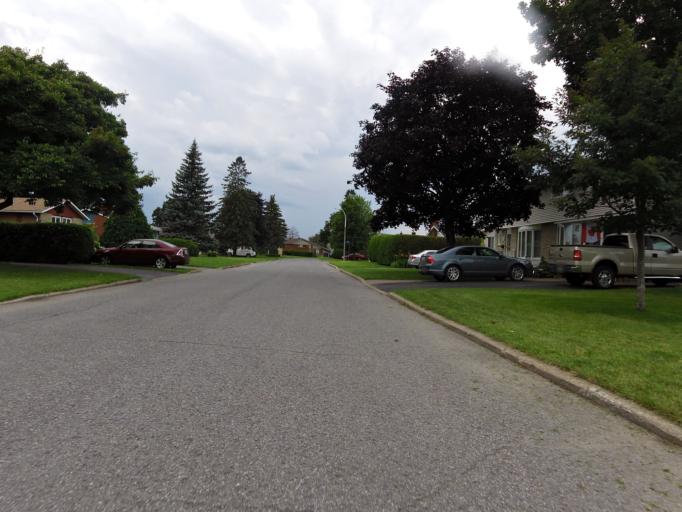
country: CA
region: Ontario
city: Ottawa
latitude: 45.3422
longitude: -75.7361
